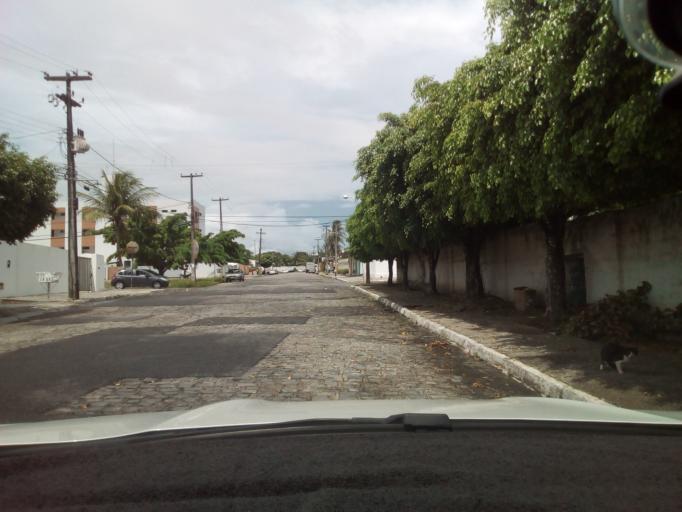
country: BR
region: Paraiba
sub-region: Joao Pessoa
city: Joao Pessoa
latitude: -7.1441
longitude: -34.8354
